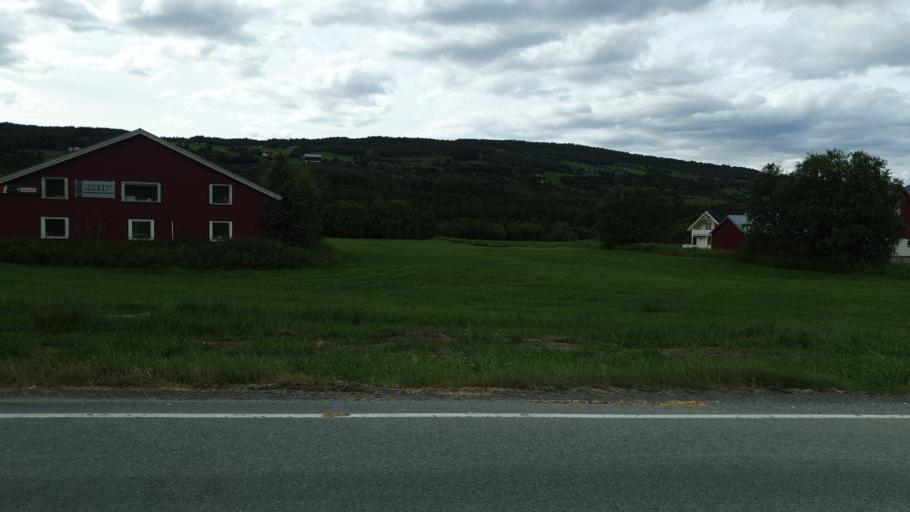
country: NO
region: Sor-Trondelag
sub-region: Oppdal
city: Oppdal
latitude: 62.5617
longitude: 9.6413
